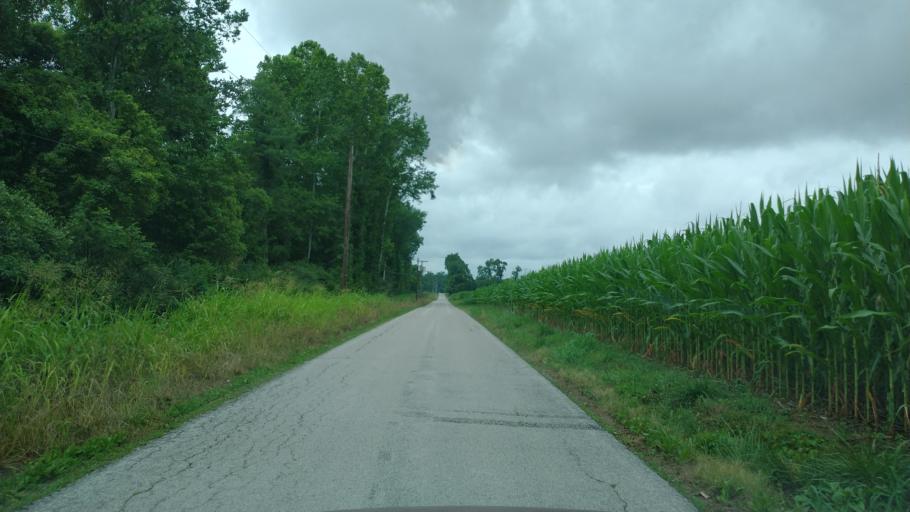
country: US
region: Ohio
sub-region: Meigs County
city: Middleport
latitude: 38.9350
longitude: -82.0873
